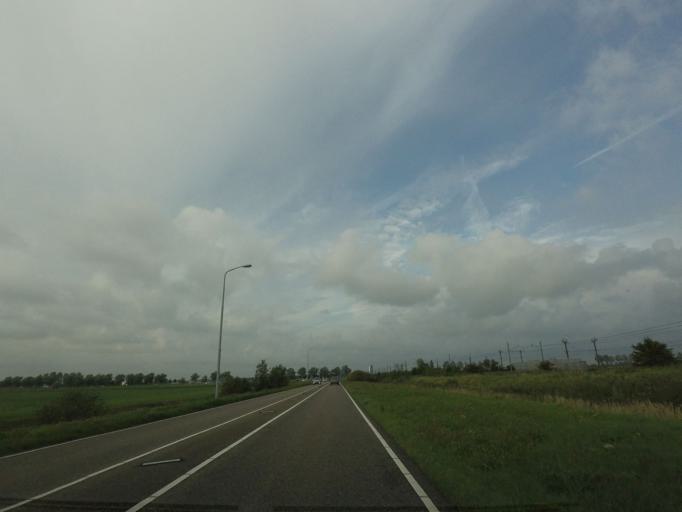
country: NL
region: North Holland
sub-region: Gemeente Haarlemmermeer
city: Hoofddorp
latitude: 52.2757
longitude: 4.6685
